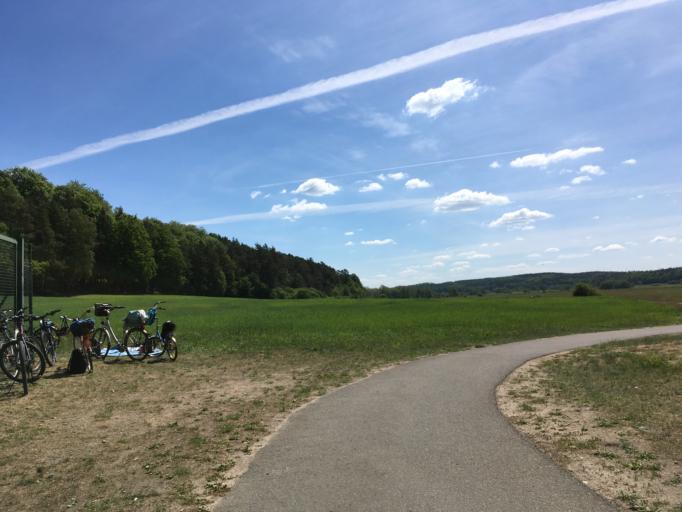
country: DE
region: Brandenburg
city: Niederfinow
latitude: 52.8500
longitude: 13.8837
